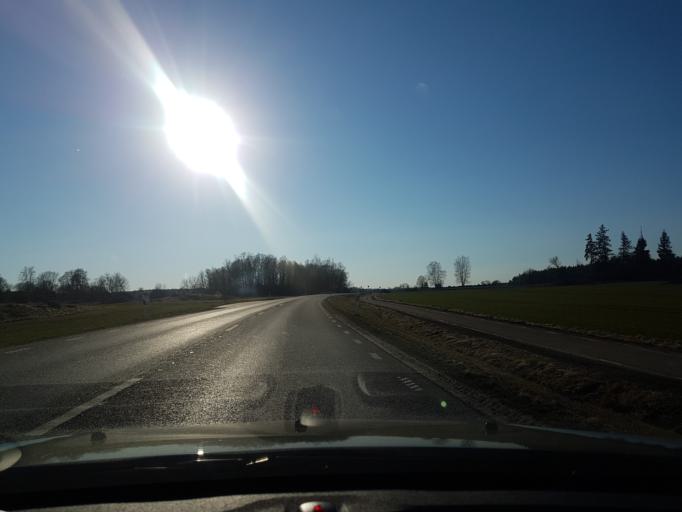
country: SE
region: Uppsala
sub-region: Uppsala Kommun
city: Uppsala
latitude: 59.8509
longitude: 17.4581
